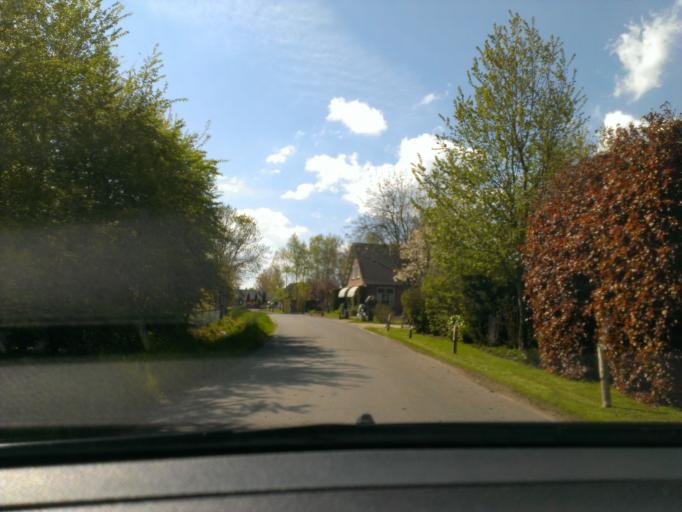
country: NL
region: Gelderland
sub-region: Gemeente Epe
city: Oene
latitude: 52.3530
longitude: 6.0596
